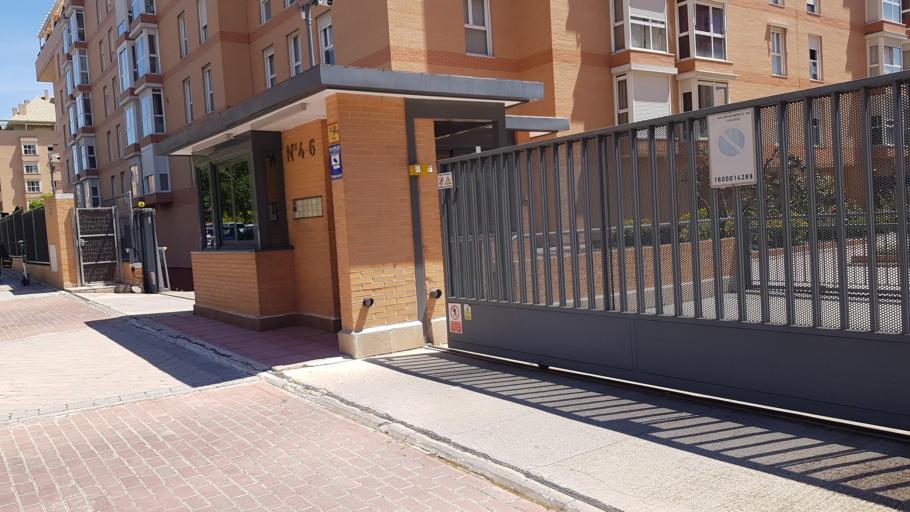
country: ES
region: Madrid
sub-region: Provincia de Madrid
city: Pinar de Chamartin
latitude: 40.4910
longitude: -3.6579
